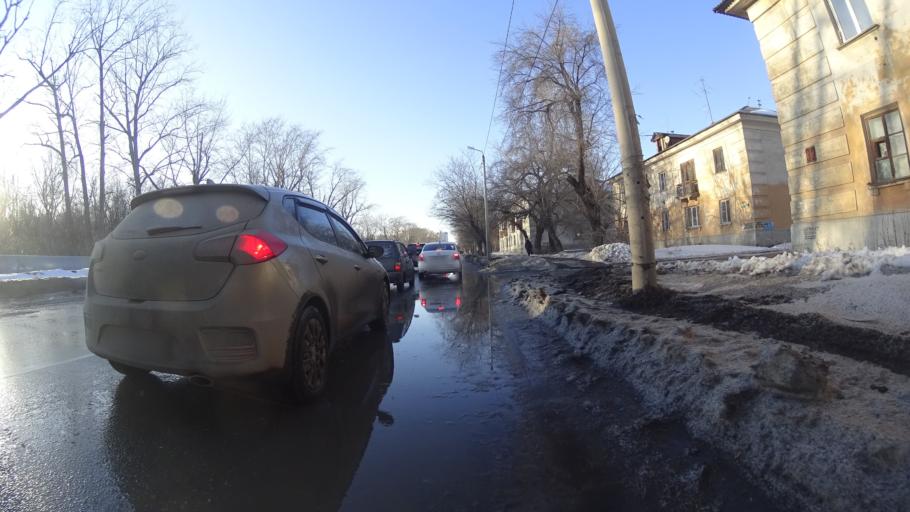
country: RU
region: Chelyabinsk
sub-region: Gorod Chelyabinsk
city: Chelyabinsk
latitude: 55.1331
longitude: 61.4608
